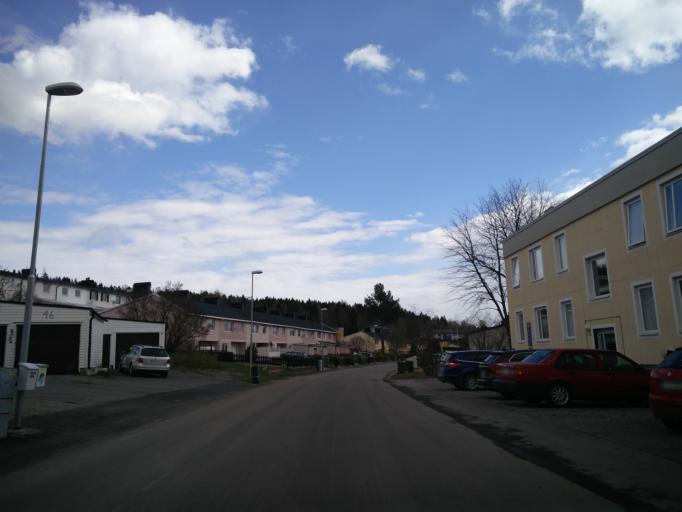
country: SE
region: Vaesternorrland
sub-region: Sundsvalls Kommun
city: Sundsvall
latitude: 62.4057
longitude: 17.2604
